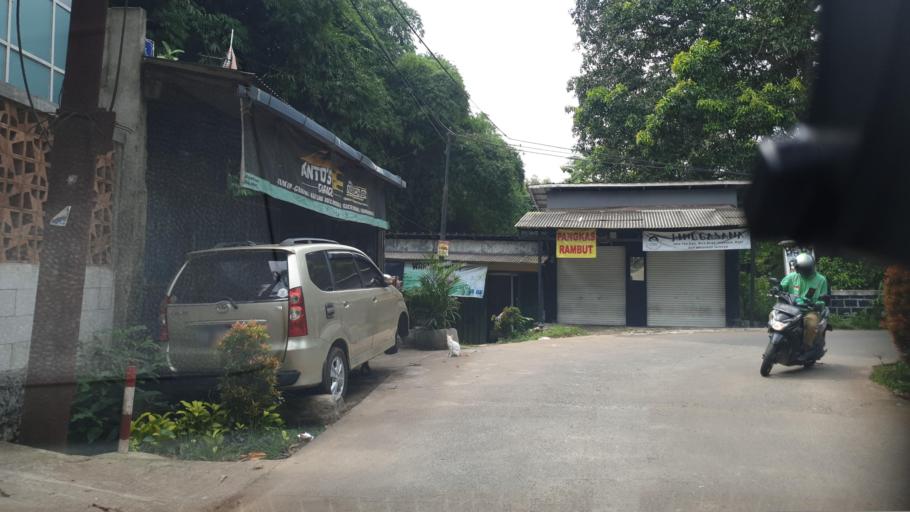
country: ID
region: West Java
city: Pamulang
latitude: -6.3480
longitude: 106.7740
